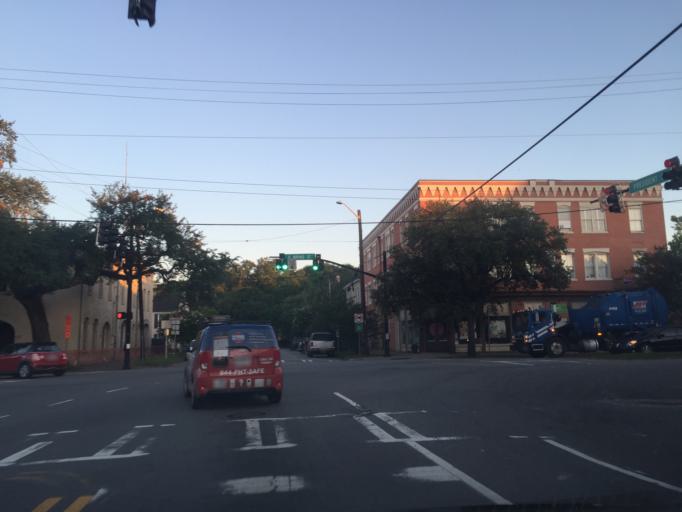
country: US
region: Georgia
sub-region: Chatham County
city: Savannah
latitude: 32.0760
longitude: -81.0849
